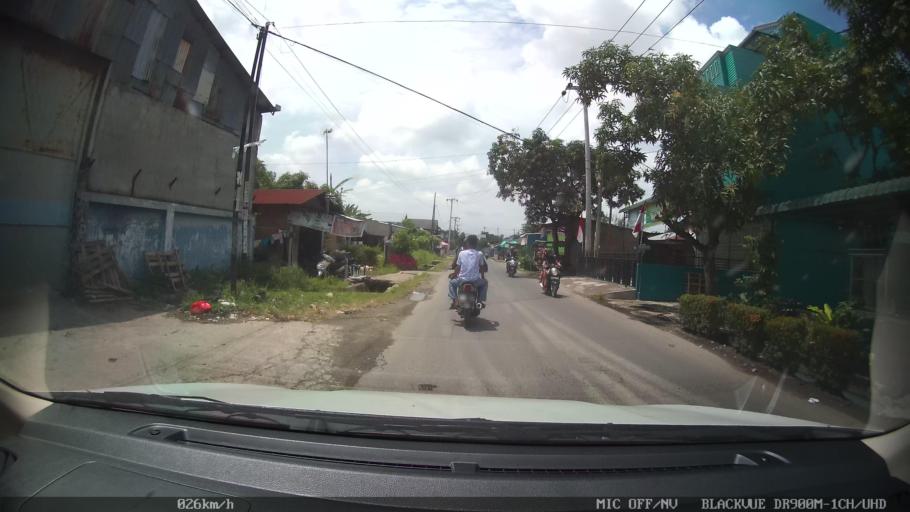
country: ID
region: North Sumatra
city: Medan
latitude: 3.6026
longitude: 98.7471
